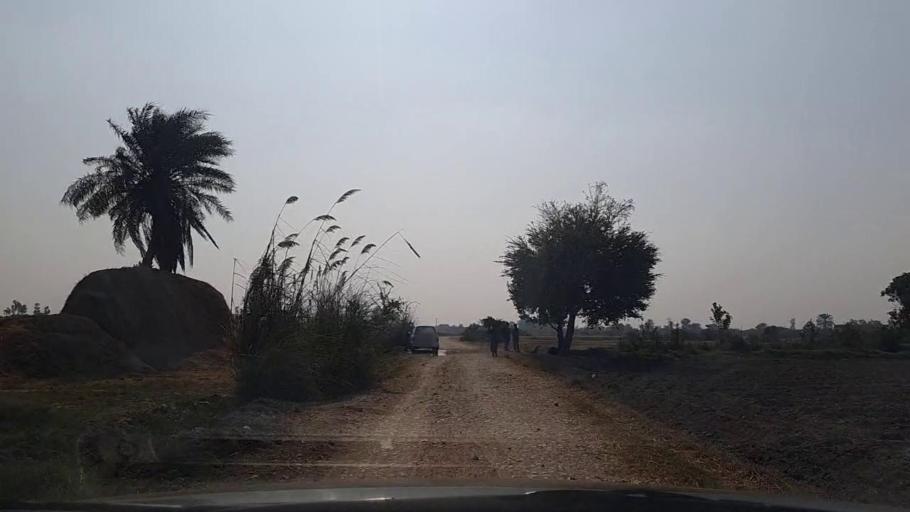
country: PK
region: Sindh
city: Mirpur Sakro
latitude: 24.5656
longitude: 67.7776
